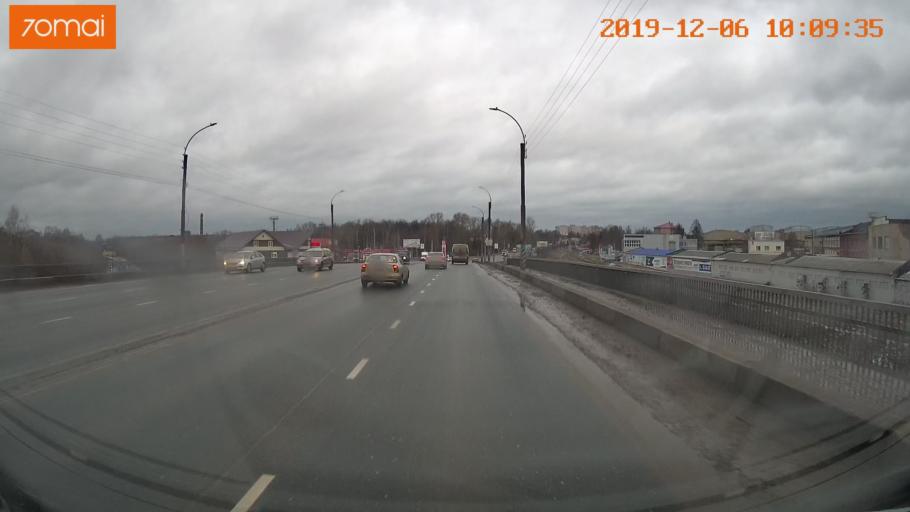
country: RU
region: Ivanovo
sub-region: Gorod Ivanovo
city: Ivanovo
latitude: 57.0248
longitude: 40.9671
